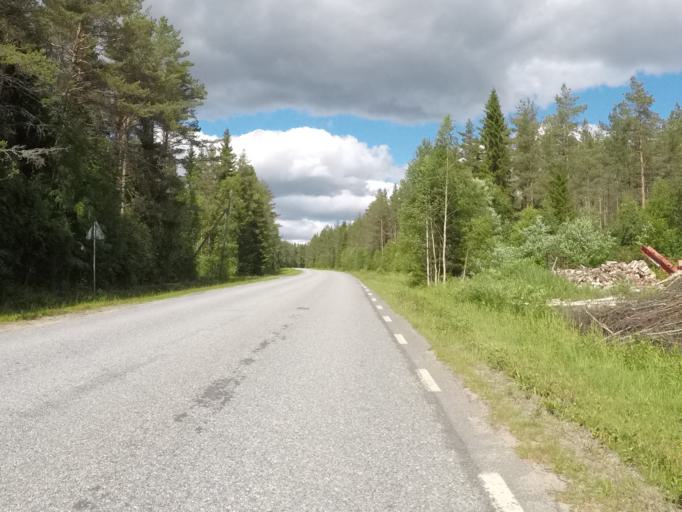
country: SE
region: Vaesterbotten
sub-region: Robertsfors Kommun
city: Robertsfors
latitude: 63.9702
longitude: 20.8119
